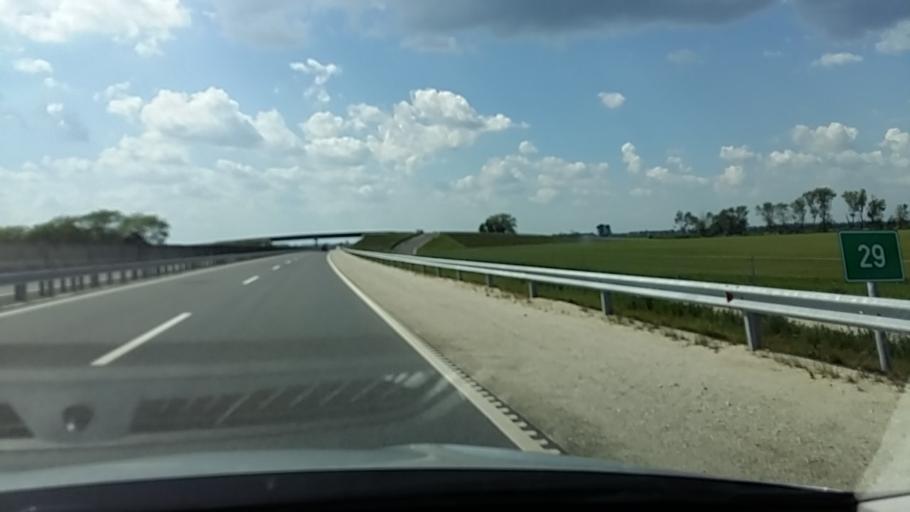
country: HU
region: Gyor-Moson-Sopron
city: Farad
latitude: 47.5822
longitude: 17.2227
